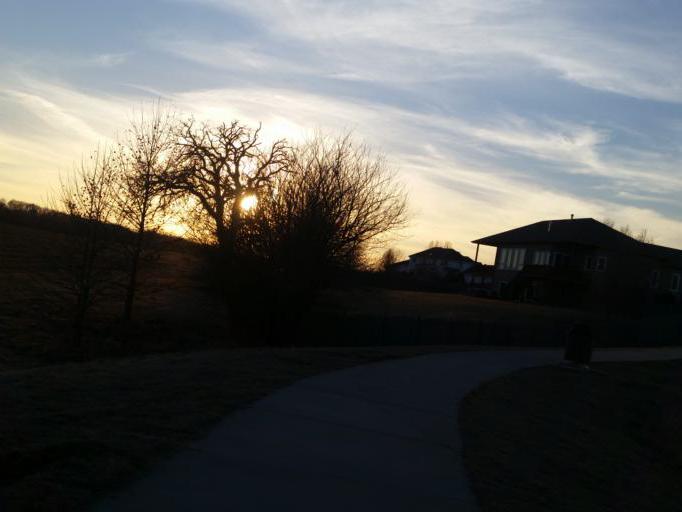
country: US
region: Nebraska
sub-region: Sarpy County
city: Papillion
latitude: 41.1514
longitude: -95.9974
